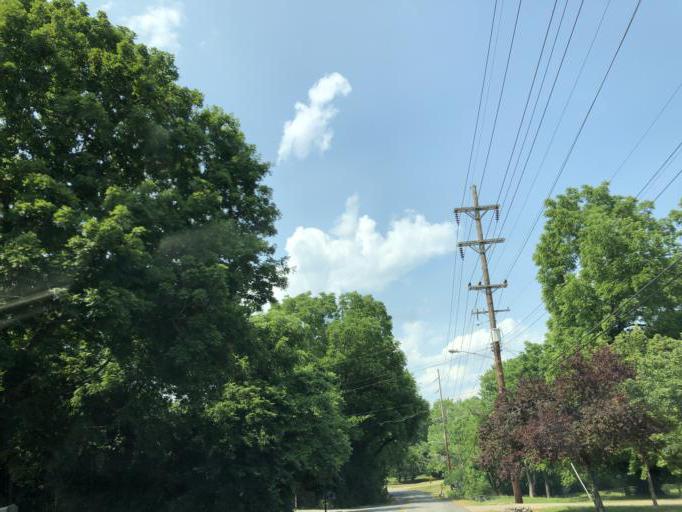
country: US
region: Tennessee
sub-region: Davidson County
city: Goodlettsville
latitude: 36.2510
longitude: -86.7225
